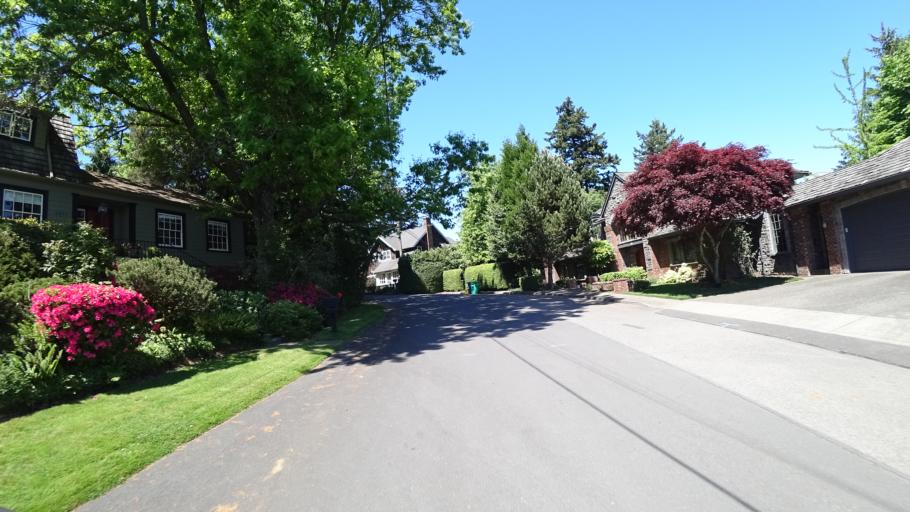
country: US
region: Oregon
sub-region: Multnomah County
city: Portland
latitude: 45.5025
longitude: -122.7156
